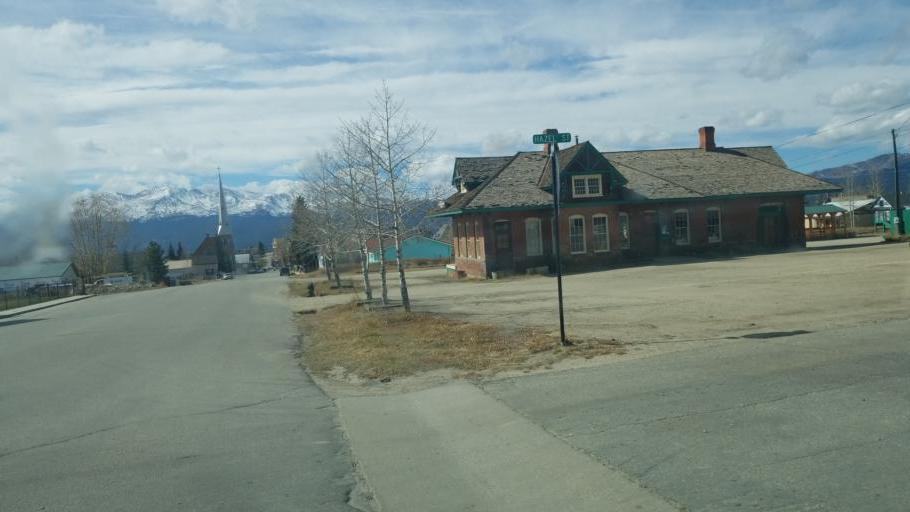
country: US
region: Colorado
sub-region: Lake County
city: Leadville
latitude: 39.2508
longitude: -106.2870
